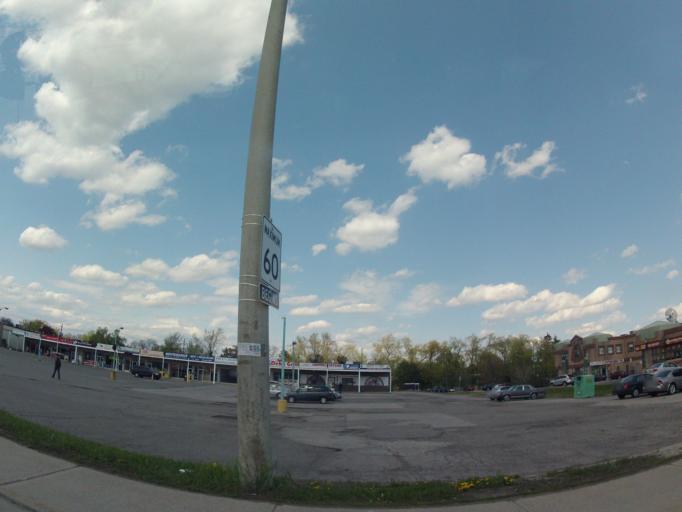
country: CA
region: Ontario
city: Mississauga
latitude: 43.5890
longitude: -79.7235
